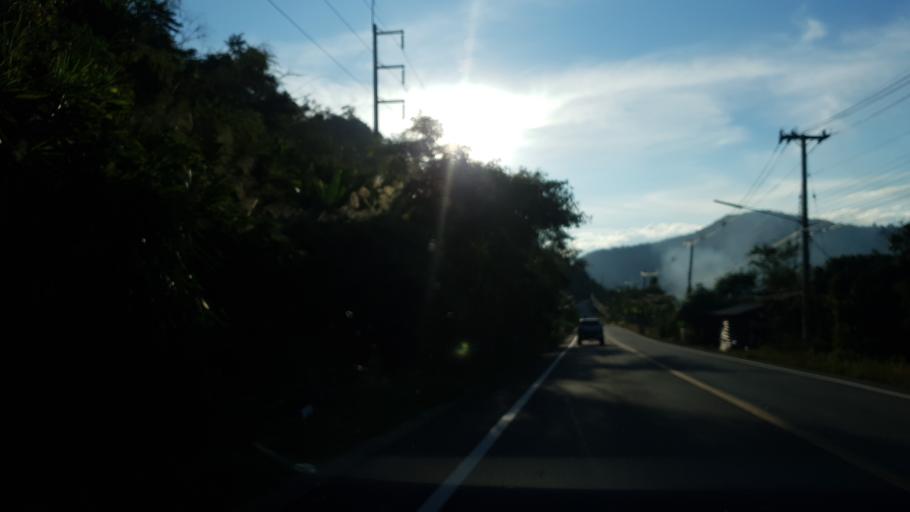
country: TH
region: Loei
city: Dan Sai
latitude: 17.2295
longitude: 101.0463
